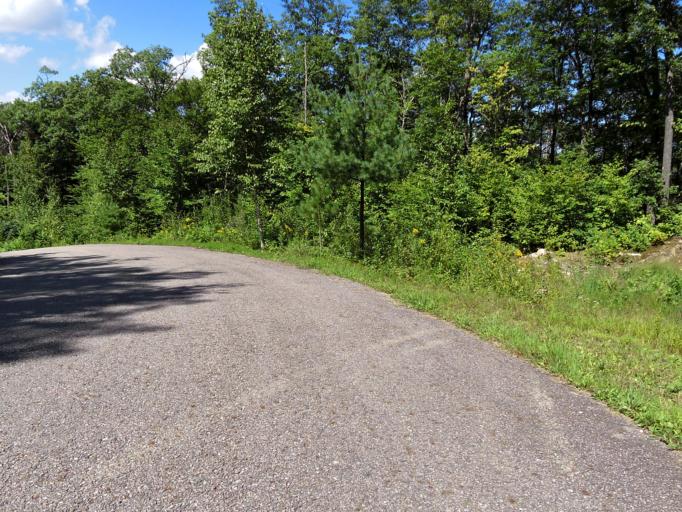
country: CA
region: Quebec
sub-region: Outaouais
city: Maniwaki
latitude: 46.2256
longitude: -76.0983
